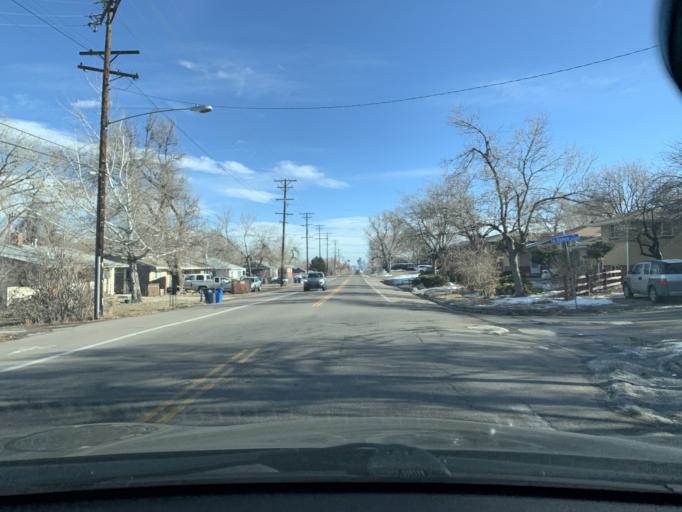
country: US
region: Colorado
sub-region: Jefferson County
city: Edgewater
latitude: 39.7475
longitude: -105.0793
